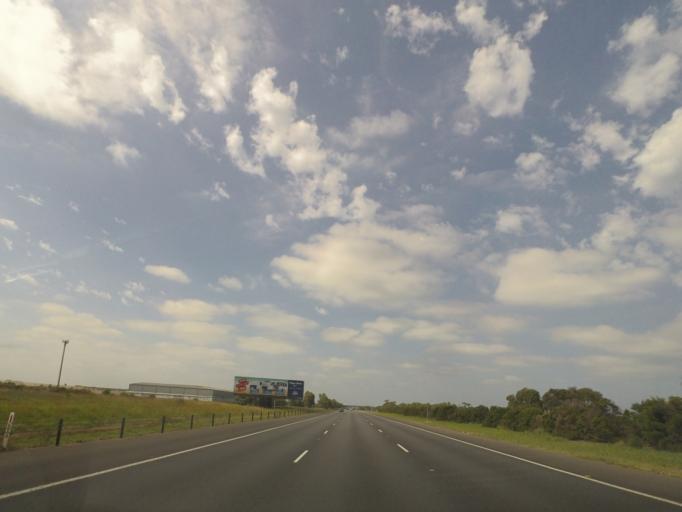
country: AU
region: Victoria
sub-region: Frankston
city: Sandhurst
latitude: -38.0455
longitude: 145.1867
